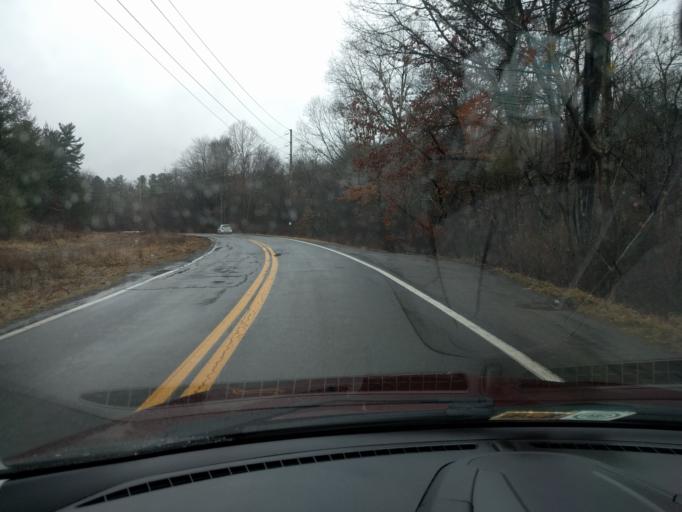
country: US
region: West Virginia
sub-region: Raleigh County
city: Beckley
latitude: 37.7960
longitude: -81.2025
